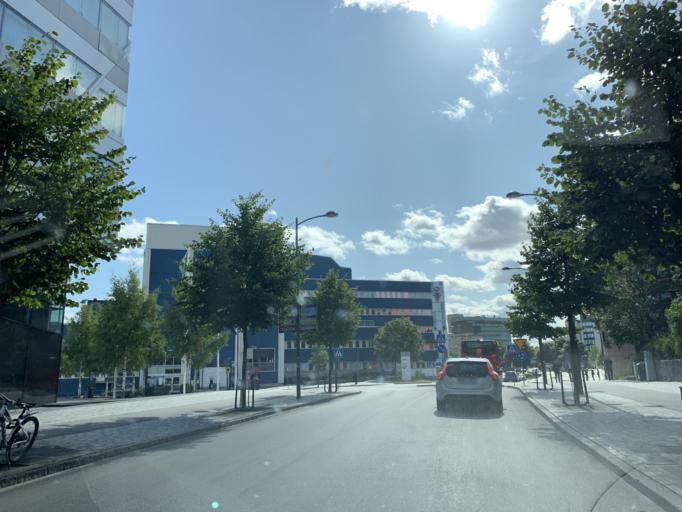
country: SE
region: Stockholm
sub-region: Sundbybergs Kommun
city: Sundbyberg
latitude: 59.3586
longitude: 17.9746
